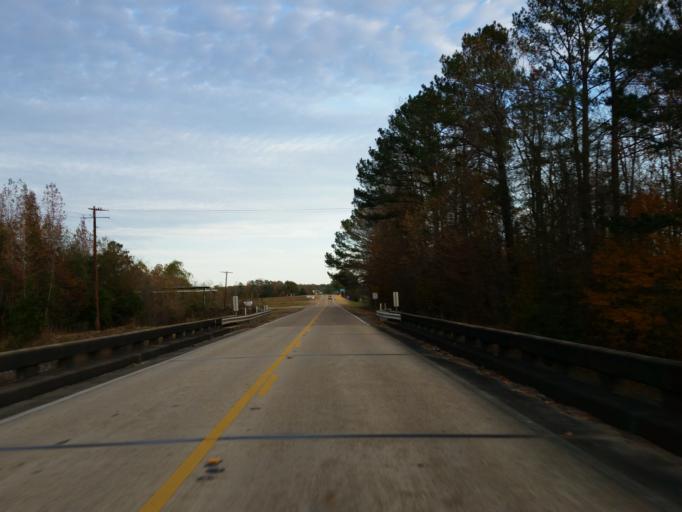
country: US
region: Alabama
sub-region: Sumter County
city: York
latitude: 32.4266
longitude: -88.4584
